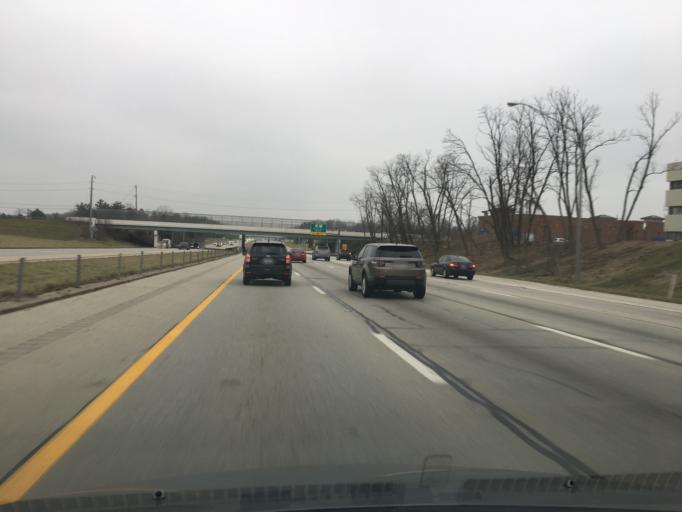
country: US
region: Ohio
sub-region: Hamilton County
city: Sixteen Mile Stand
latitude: 39.2627
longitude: -84.3401
